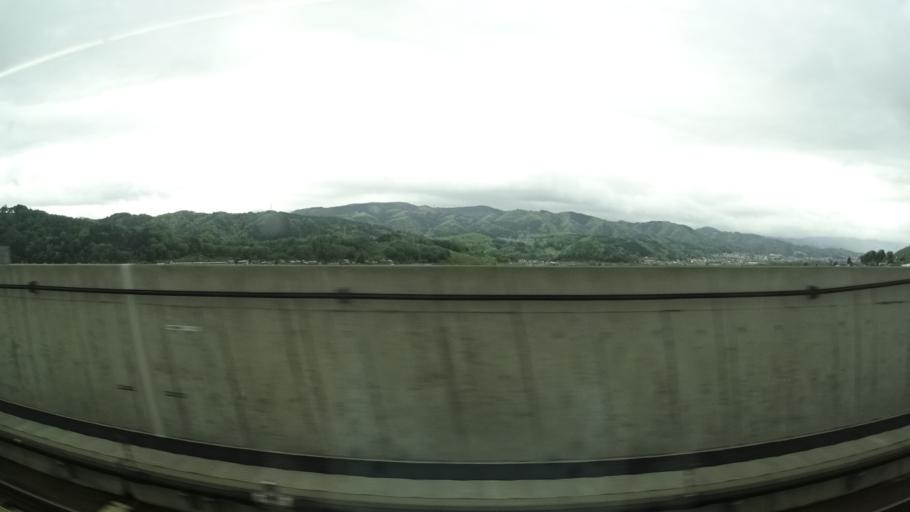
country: JP
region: Nagano
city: Nakano
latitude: 36.7923
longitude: 138.3620
